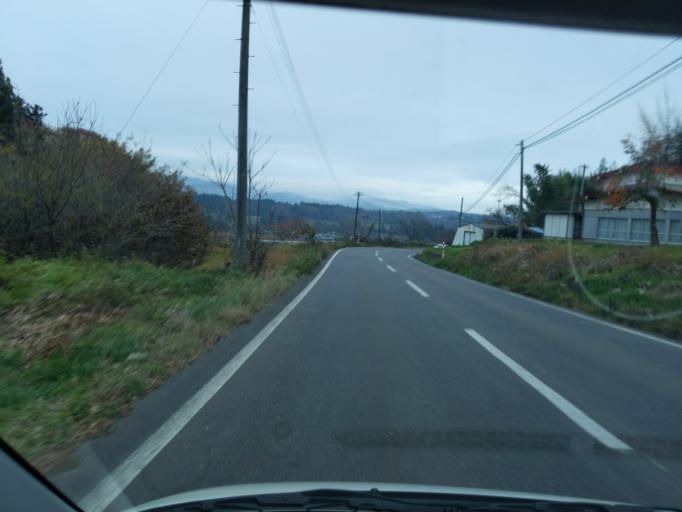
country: JP
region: Iwate
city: Kitakami
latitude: 39.2319
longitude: 141.2367
